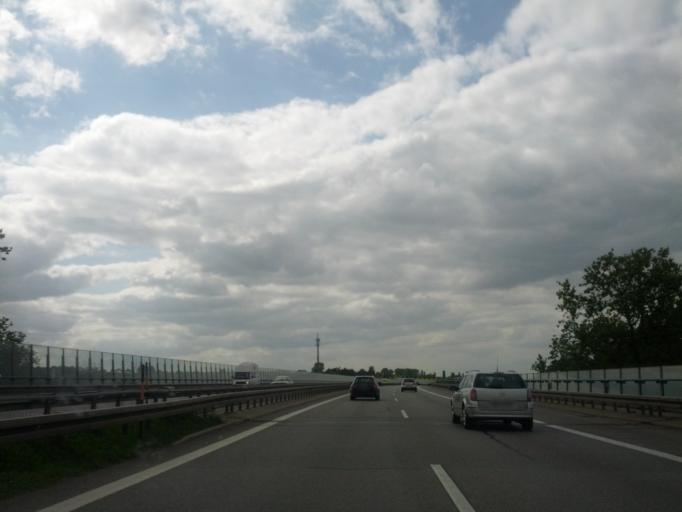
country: DE
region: Saxony
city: Kreischa
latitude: 50.9779
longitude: 13.7998
